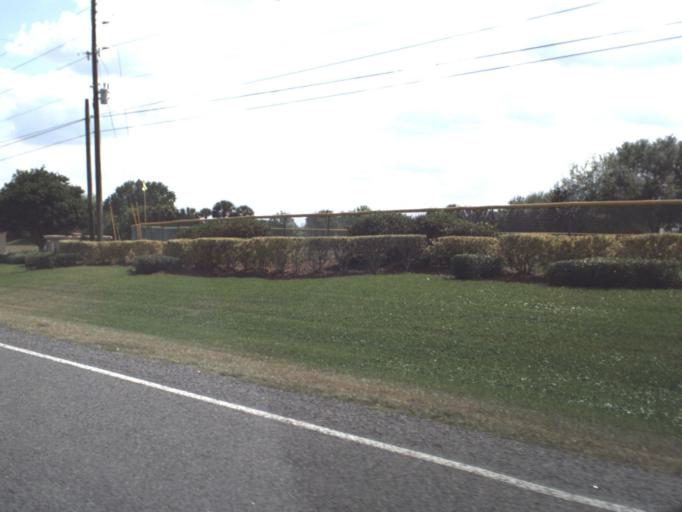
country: US
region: Florida
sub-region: Lake County
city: Yalaha
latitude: 28.6621
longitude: -81.8512
